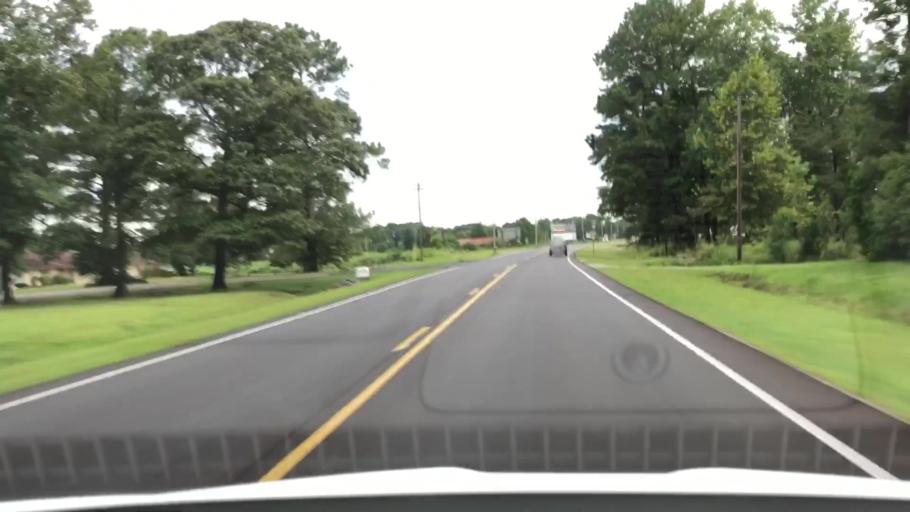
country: US
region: North Carolina
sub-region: Jones County
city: Maysville
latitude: 34.8606
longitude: -77.1883
